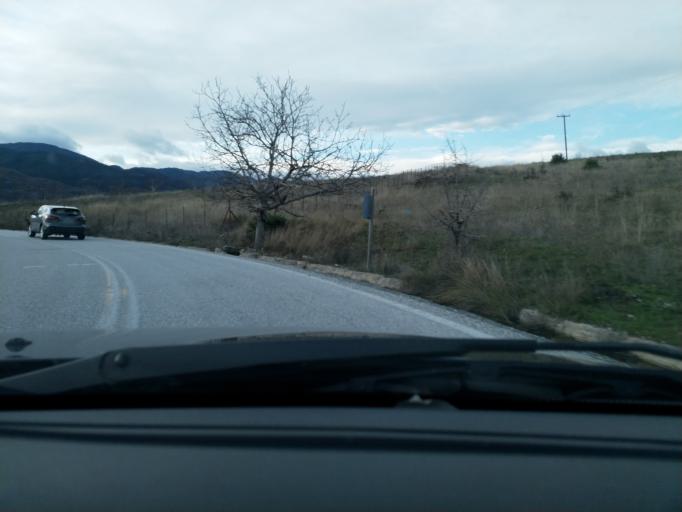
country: GR
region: Epirus
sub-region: Nomos Ioanninon
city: Metsovo
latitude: 39.7969
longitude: 21.3645
